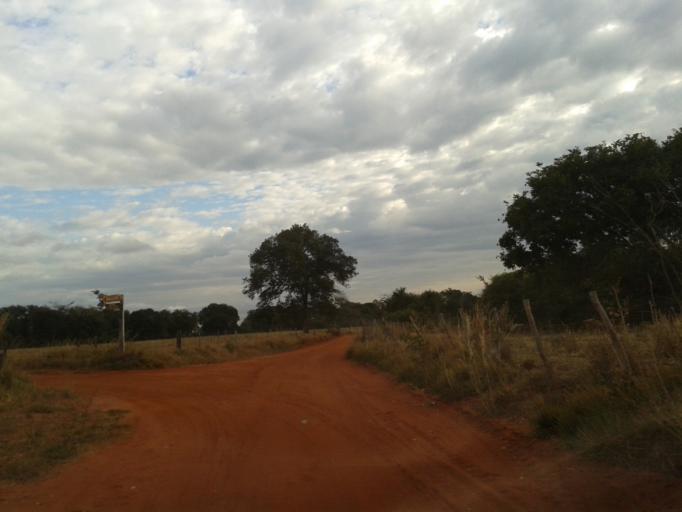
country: BR
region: Minas Gerais
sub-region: Santa Vitoria
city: Santa Vitoria
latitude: -18.7717
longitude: -50.1876
